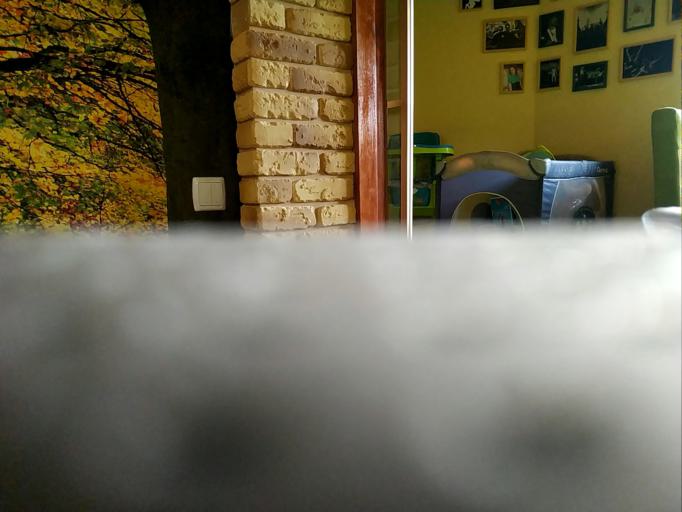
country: RU
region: Kaluga
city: Seredeyskiy
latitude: 54.0453
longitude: 35.3003
